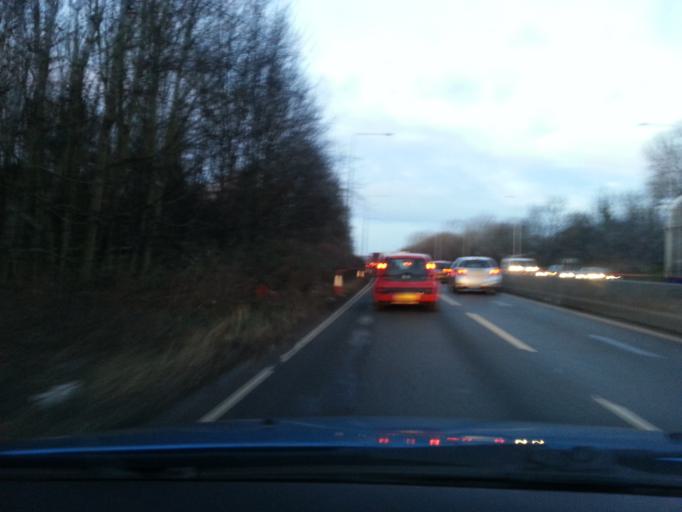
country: GB
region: England
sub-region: Gateshead
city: Lamesley
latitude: 54.9336
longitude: -1.6281
